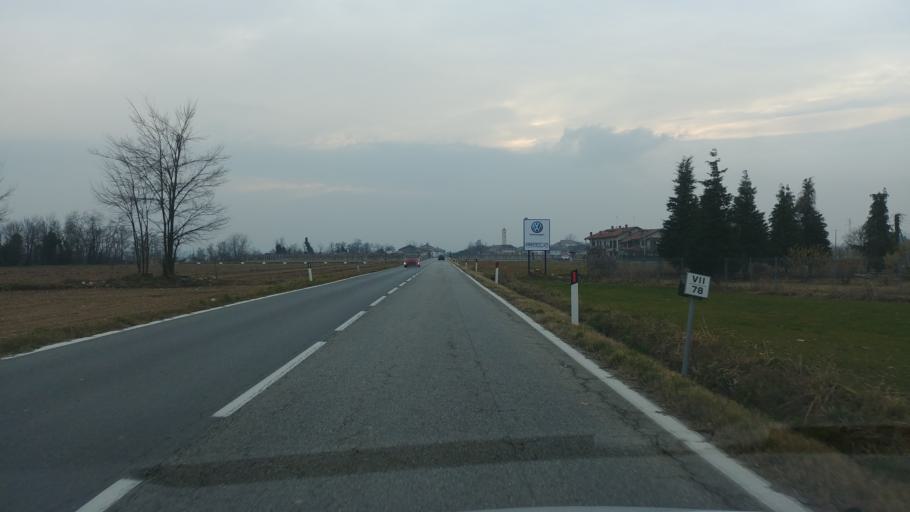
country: IT
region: Piedmont
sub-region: Provincia di Cuneo
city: Castelletto Stura
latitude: 44.4377
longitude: 7.5963
